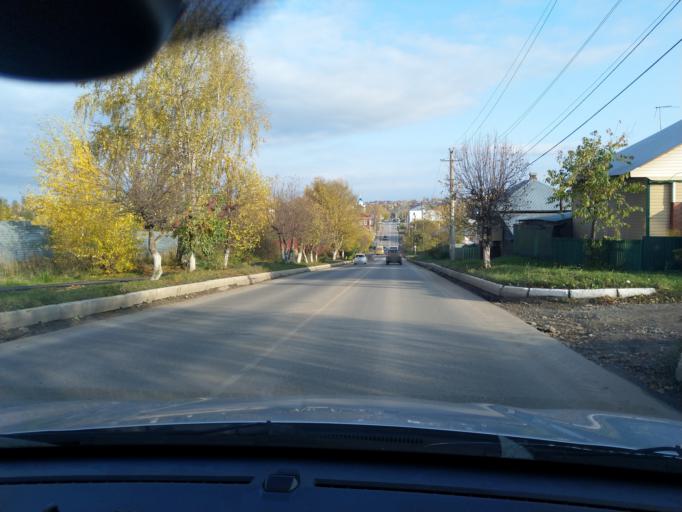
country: RU
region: Perm
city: Dobryanka
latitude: 58.4618
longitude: 56.4059
